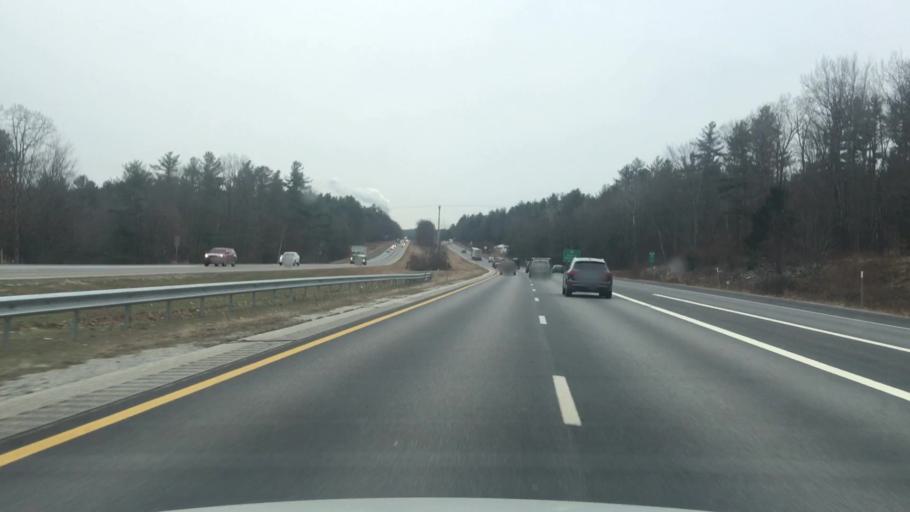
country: US
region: New Hampshire
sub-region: Merrimack County
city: Concord
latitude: 43.1778
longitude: -71.5632
